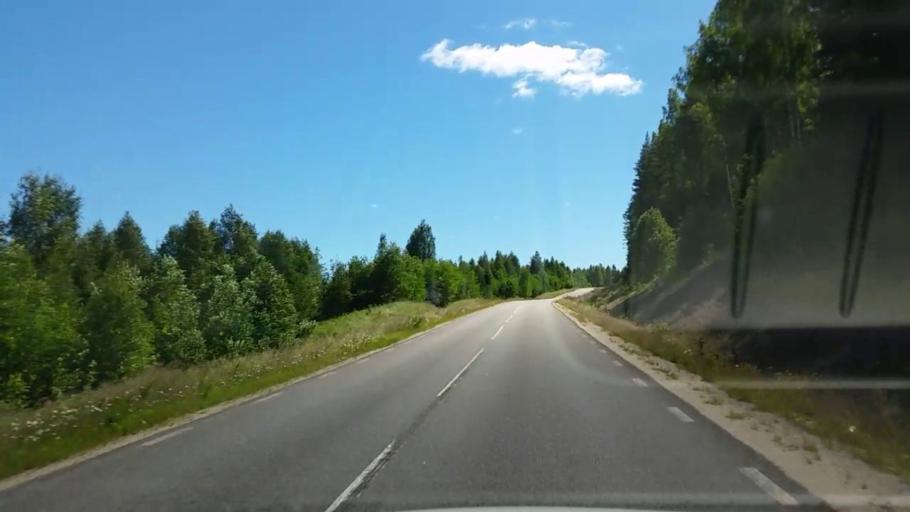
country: SE
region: Gaevleborg
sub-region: Ljusdals Kommun
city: Farila
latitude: 61.6944
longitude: 15.6485
